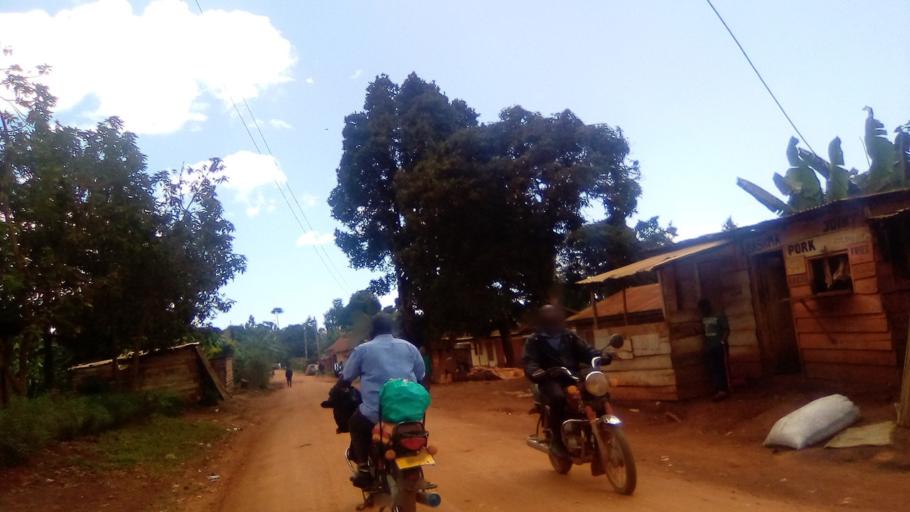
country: UG
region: Central Region
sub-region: Wakiso District
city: Entebbe
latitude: 0.1048
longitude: 32.5239
